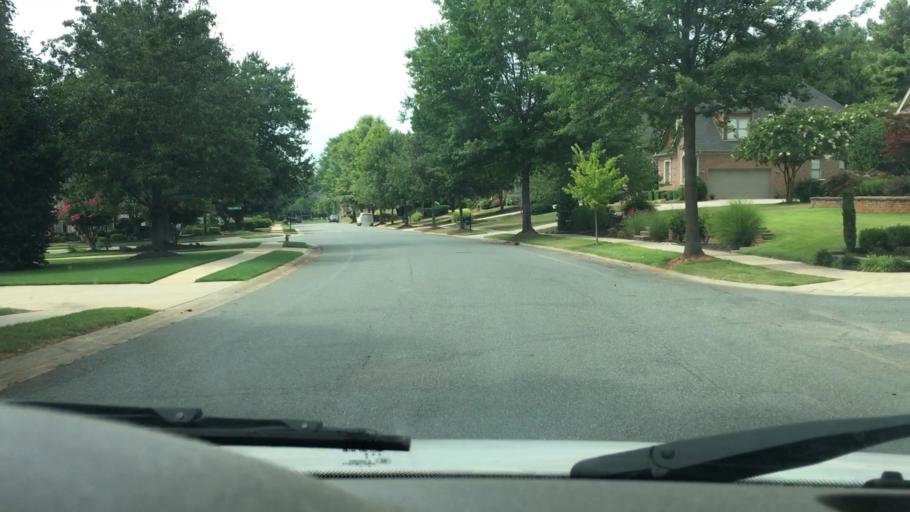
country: US
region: North Carolina
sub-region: Gaston County
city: Davidson
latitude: 35.4680
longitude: -80.7832
